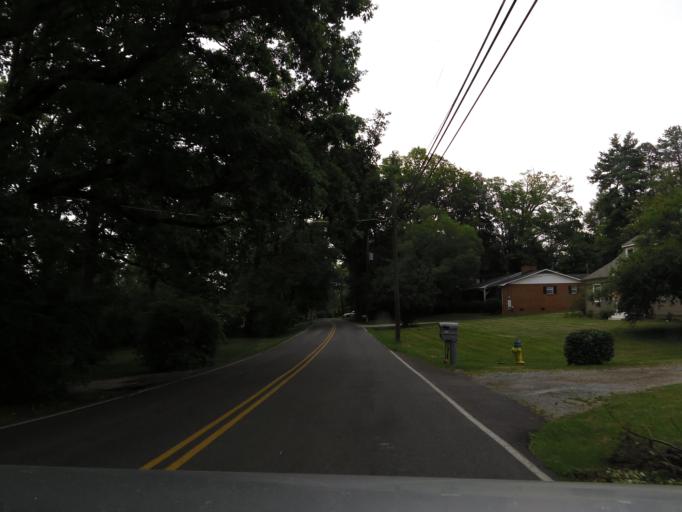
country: US
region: Tennessee
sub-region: Knox County
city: Knoxville
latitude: 35.9442
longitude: -83.9025
